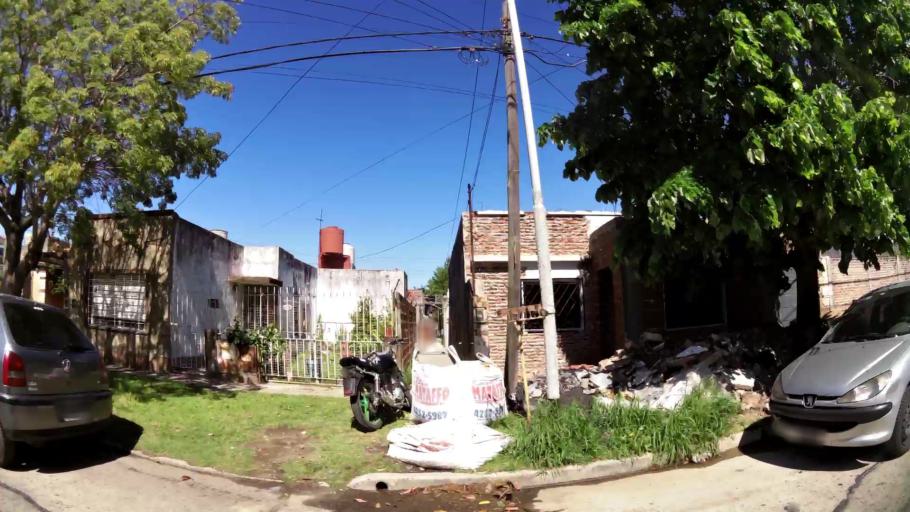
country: AR
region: Buenos Aires
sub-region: Partido de Quilmes
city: Quilmes
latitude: -34.6970
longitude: -58.3032
